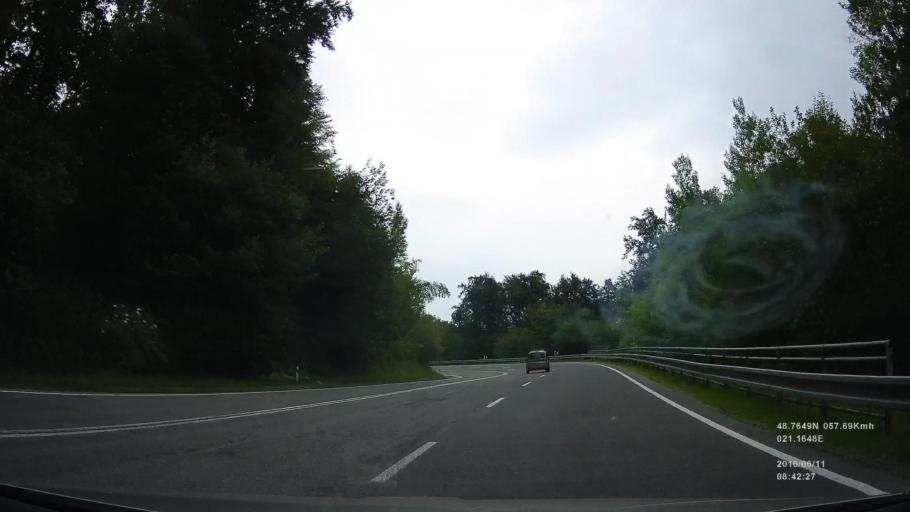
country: SK
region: Kosicky
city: Kosice
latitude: 48.7649
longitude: 21.1731
